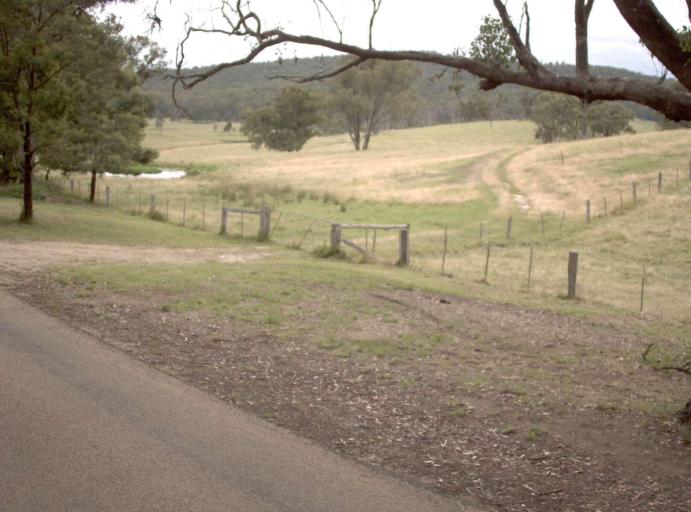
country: AU
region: Victoria
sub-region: East Gippsland
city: Bairnsdale
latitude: -37.7250
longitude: 147.5912
